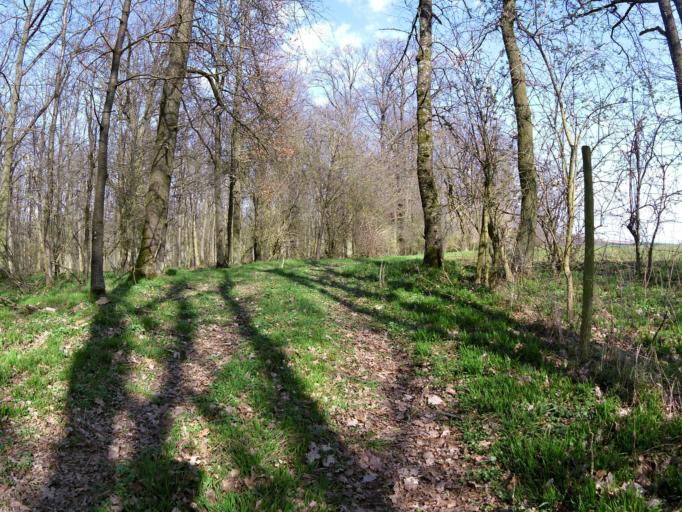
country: DE
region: Bavaria
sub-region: Regierungsbezirk Unterfranken
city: Rottendorf
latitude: 49.8027
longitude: 10.0568
